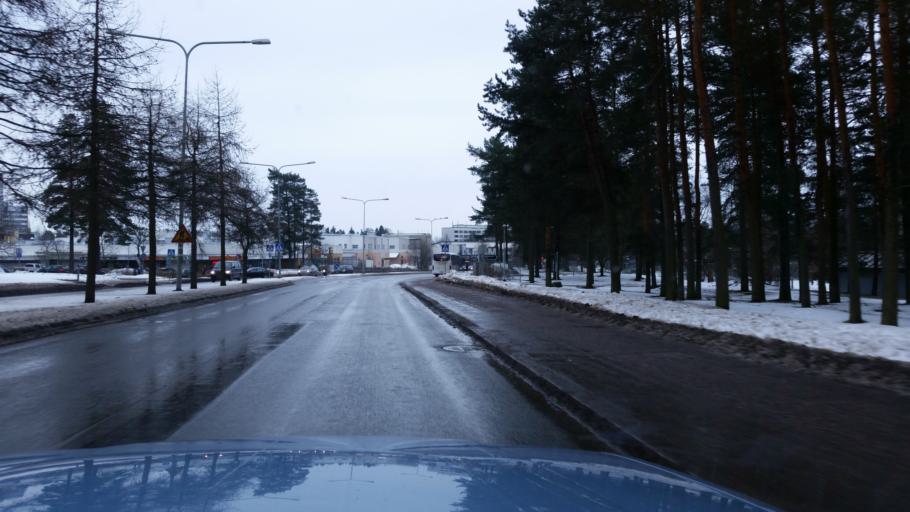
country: FI
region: Uusimaa
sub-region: Helsinki
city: Vantaa
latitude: 60.2373
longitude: 25.0798
